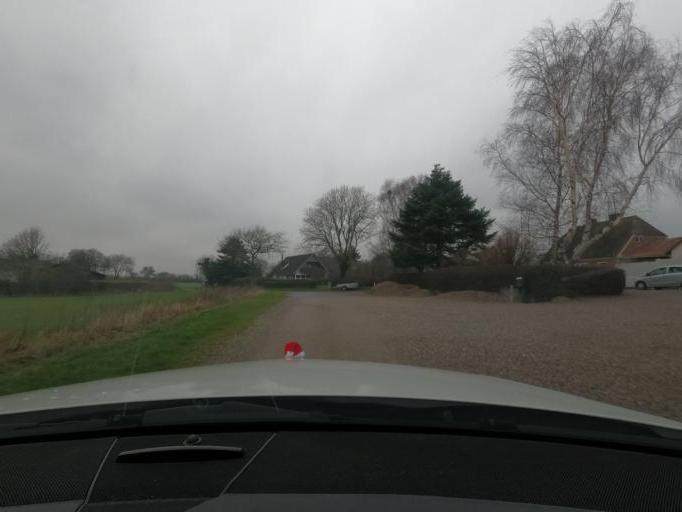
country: DK
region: South Denmark
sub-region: Haderslev Kommune
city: Starup
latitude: 55.1857
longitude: 9.6542
